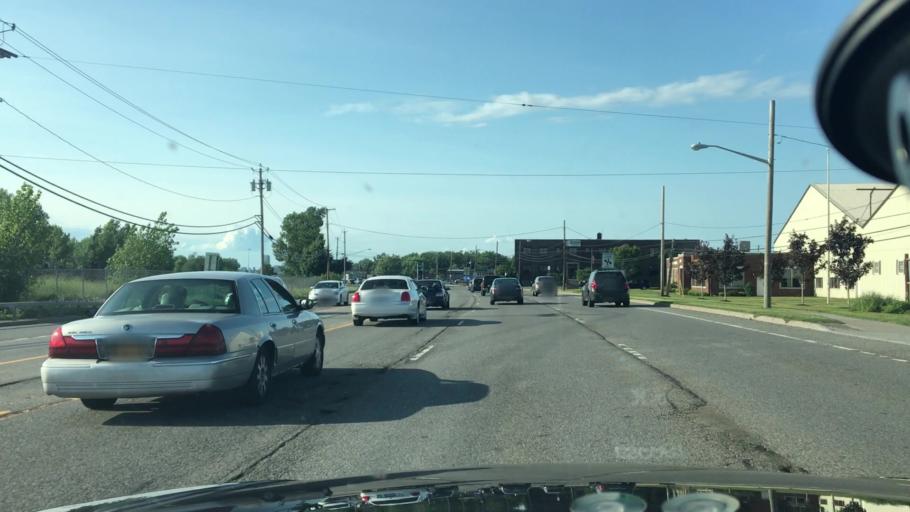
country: US
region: New York
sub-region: Erie County
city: Lackawanna
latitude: 42.8133
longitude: -78.8453
